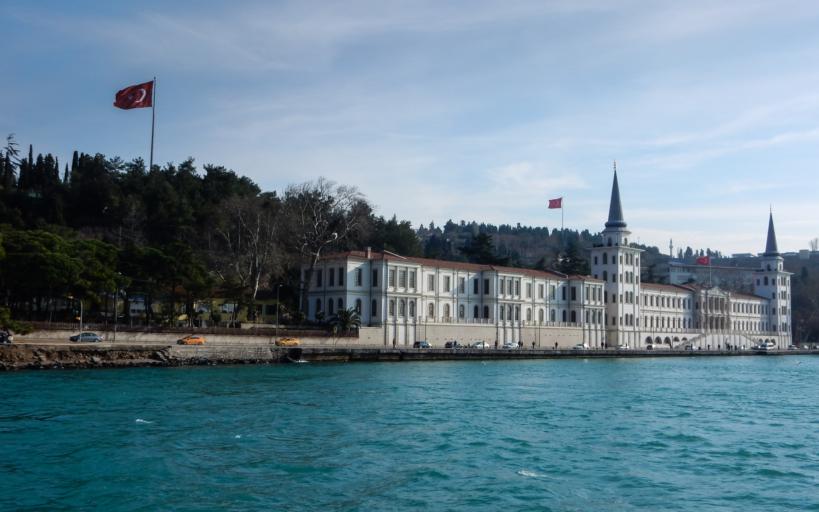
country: TR
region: Istanbul
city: UEskuedar
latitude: 41.0604
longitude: 29.0514
